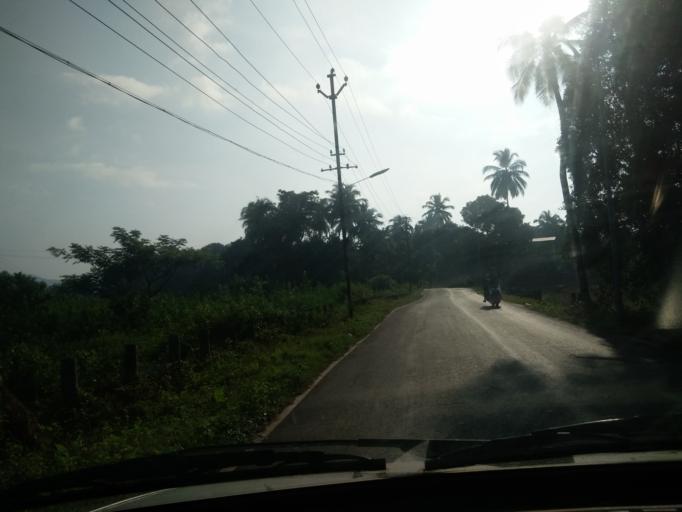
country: IN
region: Goa
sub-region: South Goa
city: Cuncolim
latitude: 15.1806
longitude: 73.9936
